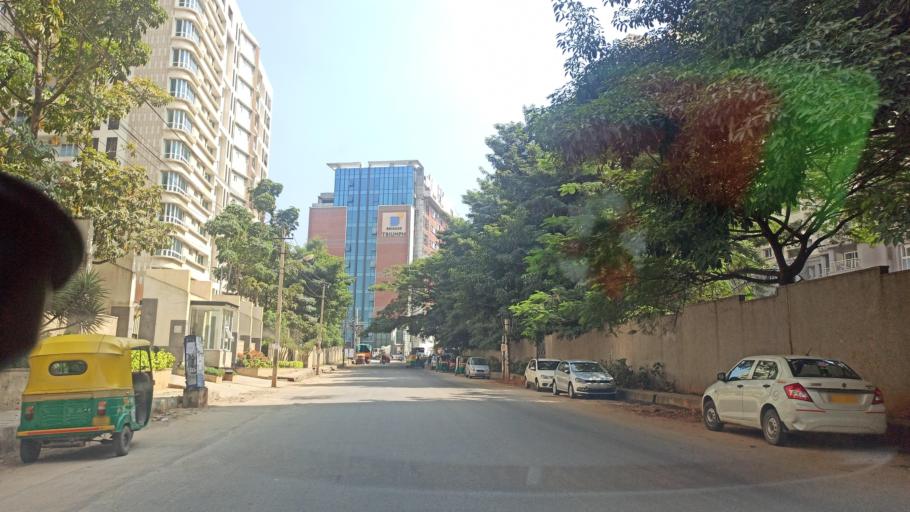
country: IN
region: Karnataka
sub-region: Bangalore Urban
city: Yelahanka
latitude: 13.0555
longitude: 77.5961
